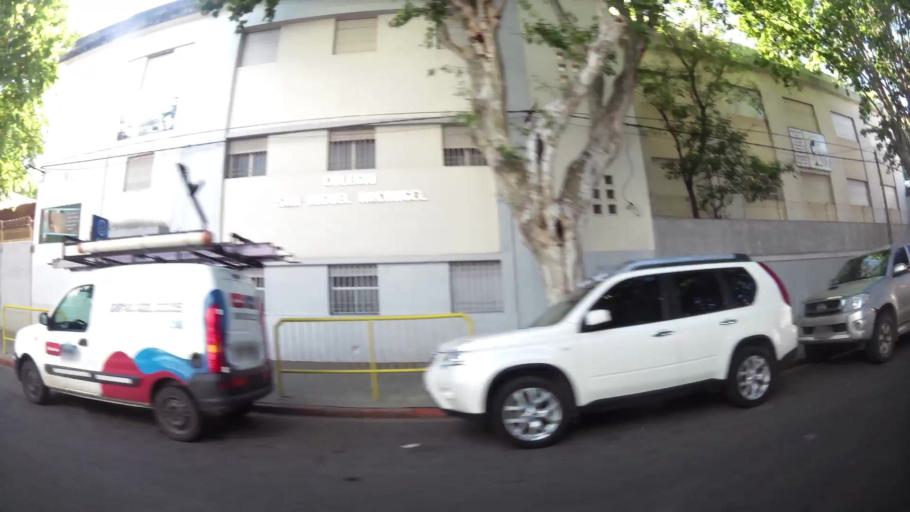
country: AR
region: Santa Fe
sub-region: Departamento de Rosario
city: Rosario
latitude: -32.9485
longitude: -60.6744
